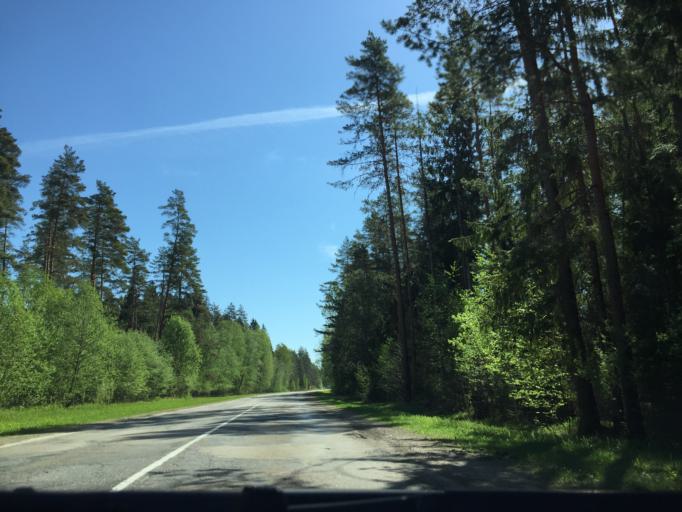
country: LV
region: Incukalns
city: Incukalns
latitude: 57.0319
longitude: 24.7030
